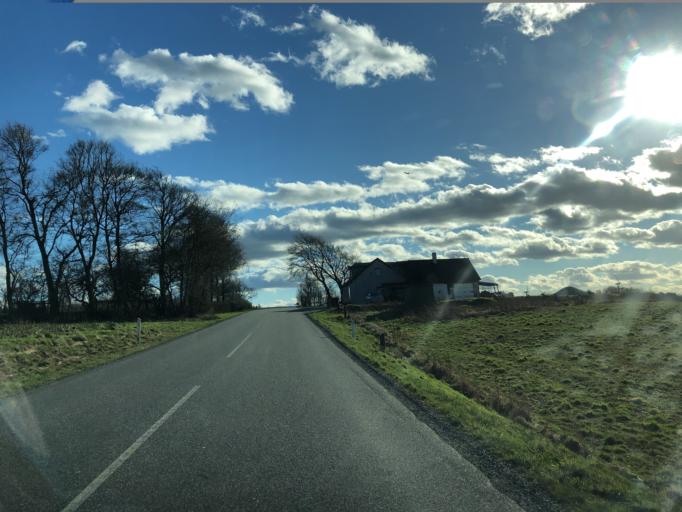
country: DK
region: Central Jutland
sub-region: Silkeborg Kommune
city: Kjellerup
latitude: 56.3200
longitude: 9.4757
